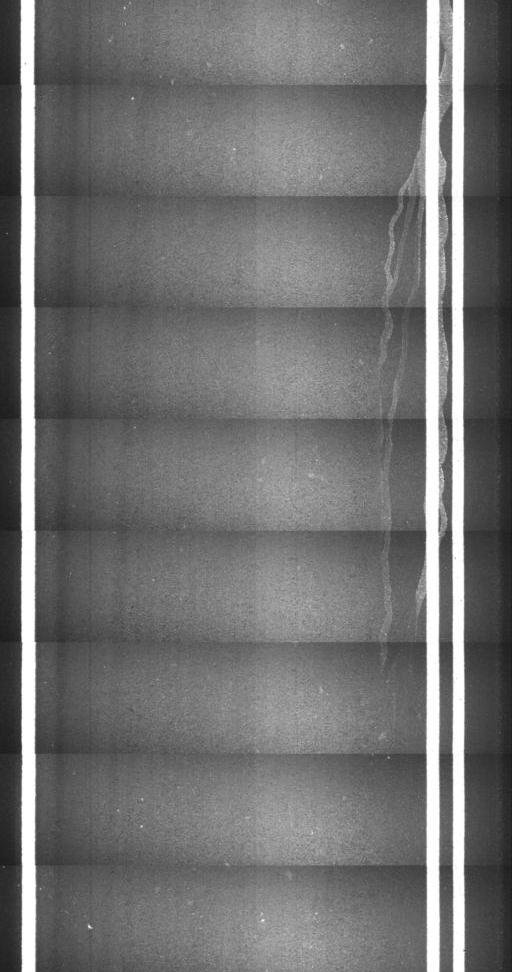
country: US
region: Vermont
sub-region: Orange County
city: Randolph
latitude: 43.9086
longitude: -72.6622
